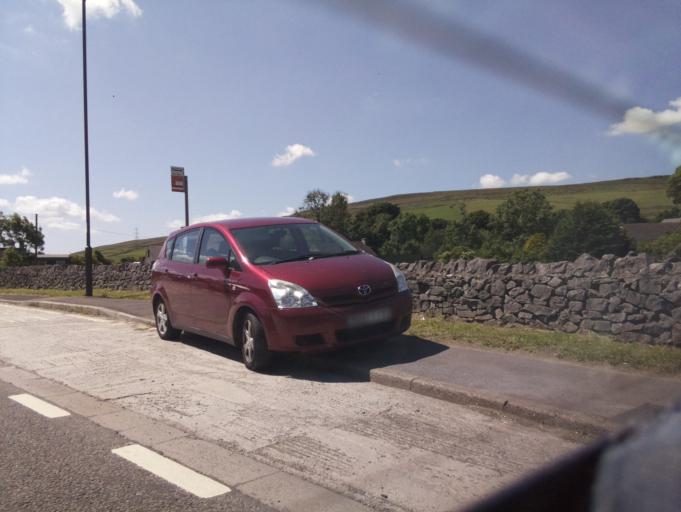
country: GB
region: England
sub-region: Derbyshire
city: Chapel en le Frith
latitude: 53.2973
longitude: -1.8882
